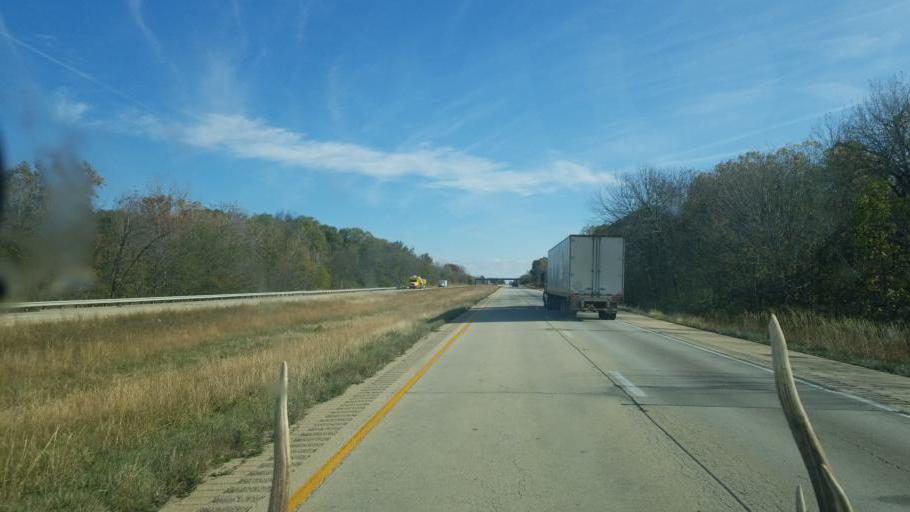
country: US
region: Illinois
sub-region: Effingham County
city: Altamont
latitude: 39.0706
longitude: -88.6599
